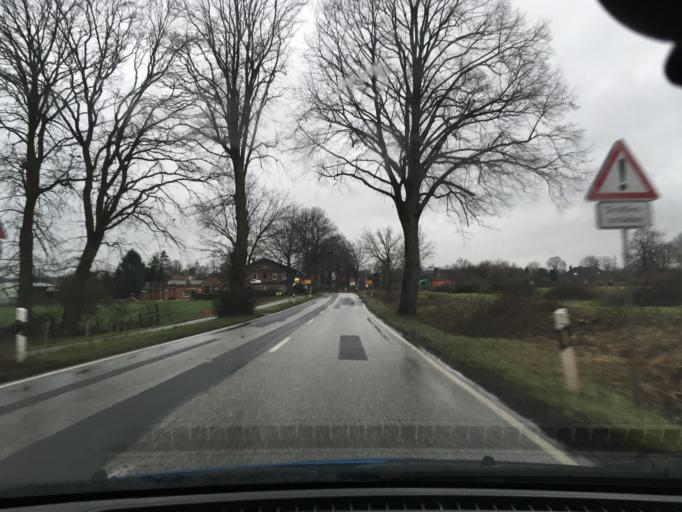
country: DE
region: Schleswig-Holstein
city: Wiershop
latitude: 53.4046
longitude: 10.4480
